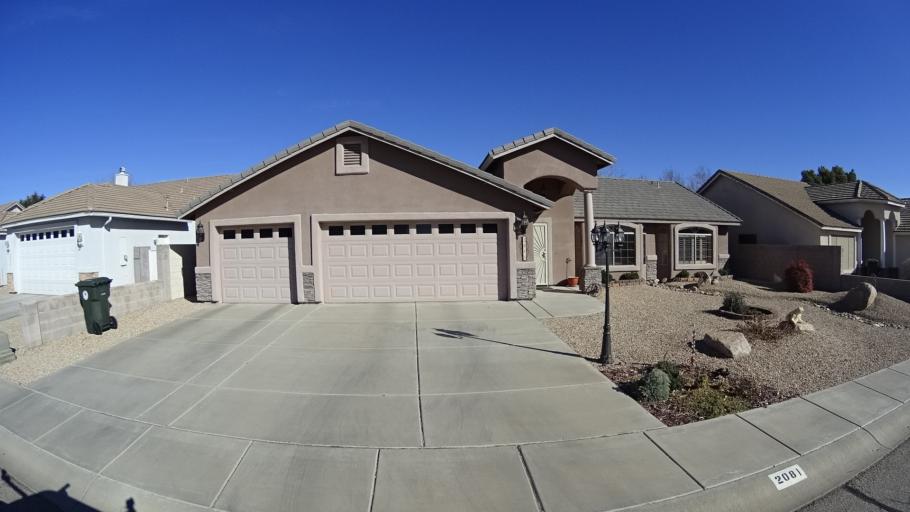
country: US
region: Arizona
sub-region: Mohave County
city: New Kingman-Butler
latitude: 35.2362
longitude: -114.0292
